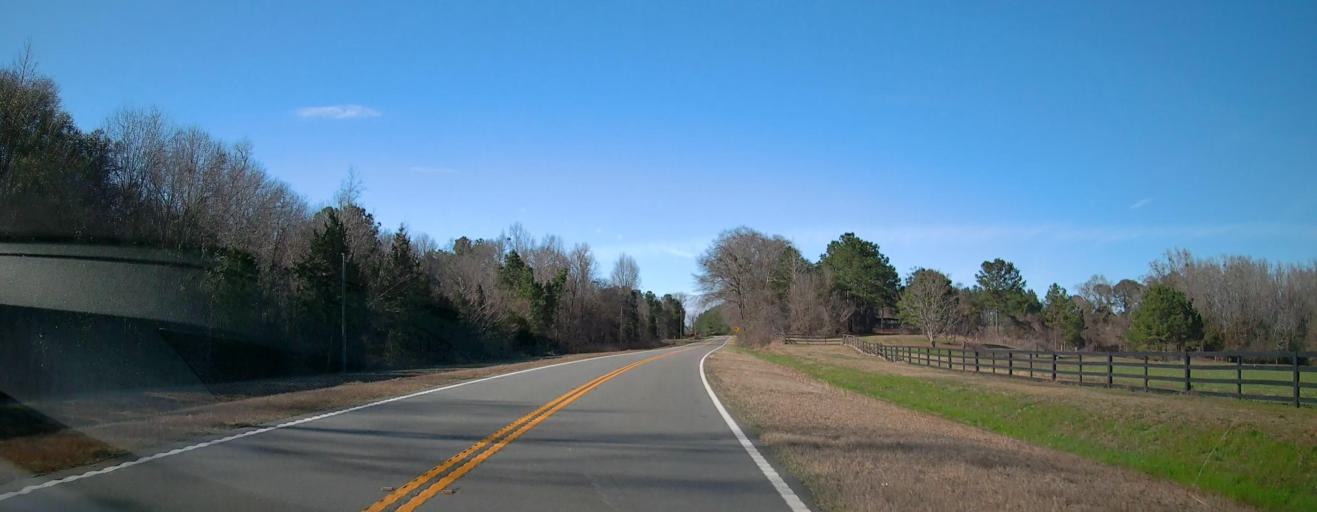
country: US
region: Georgia
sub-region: Macon County
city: Oglethorpe
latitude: 32.3804
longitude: -84.1901
